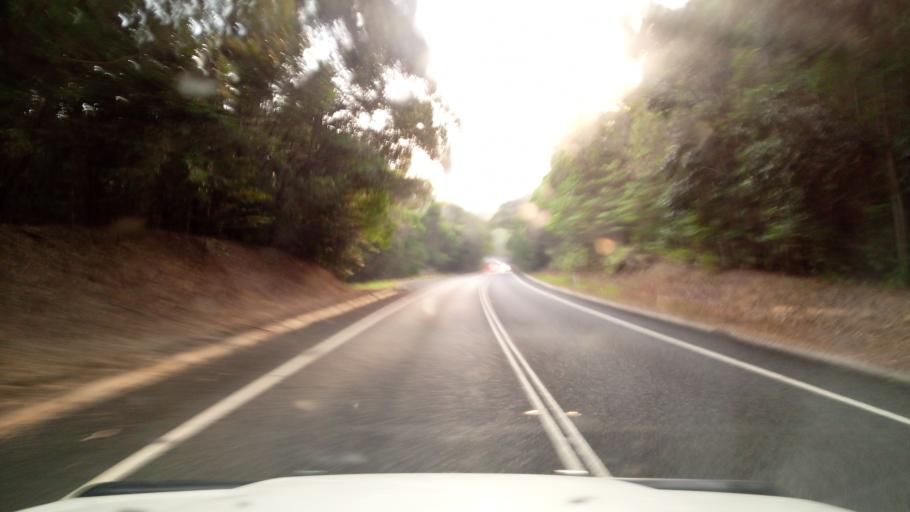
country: AU
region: Queensland
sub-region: Tablelands
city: Kuranda
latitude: -16.8453
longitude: 145.6070
